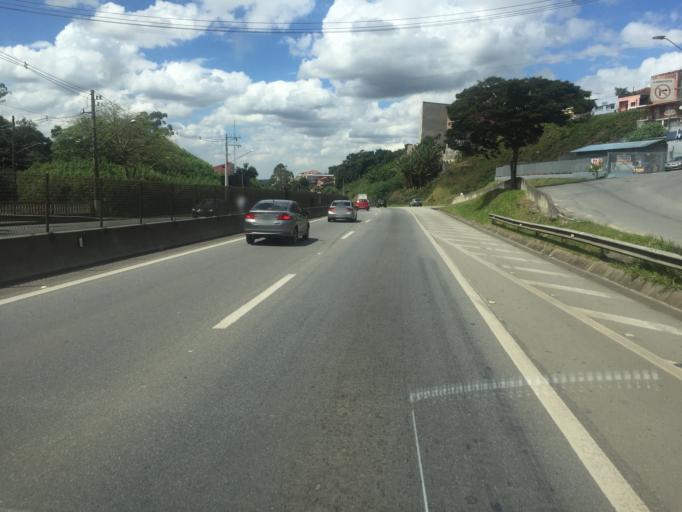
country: BR
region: Sao Paulo
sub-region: Cotia
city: Cotia
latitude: -23.6023
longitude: -46.9336
